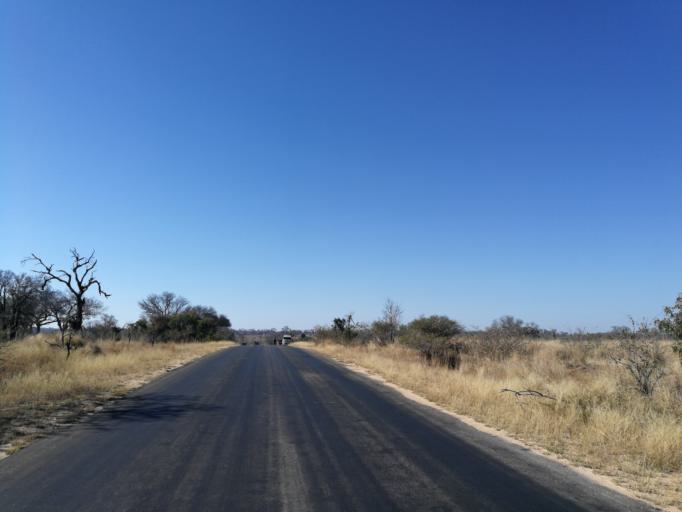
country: ZA
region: Limpopo
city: Thulamahashi
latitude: -24.9922
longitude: 31.5171
